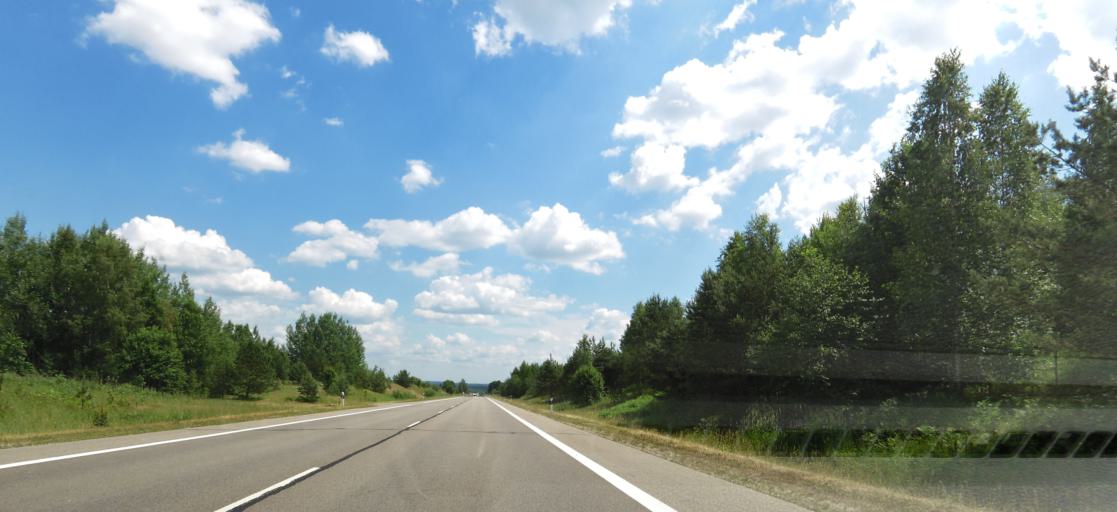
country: LT
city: Skaidiskes
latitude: 54.6065
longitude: 25.4664
